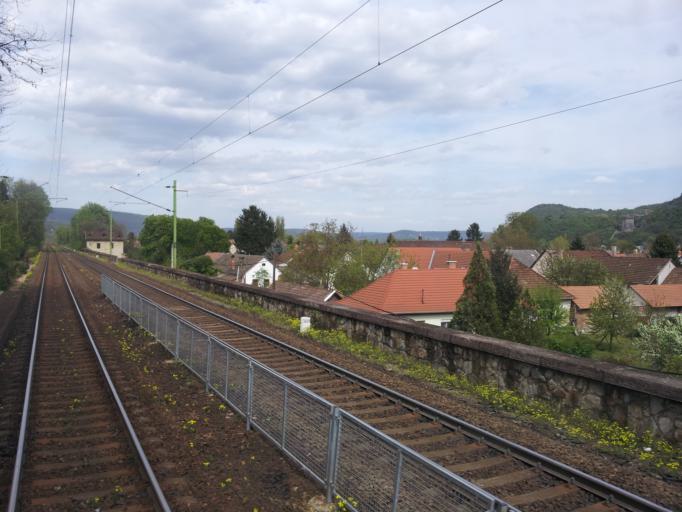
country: HU
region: Pest
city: Nagymaros
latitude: 47.7921
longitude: 18.9594
